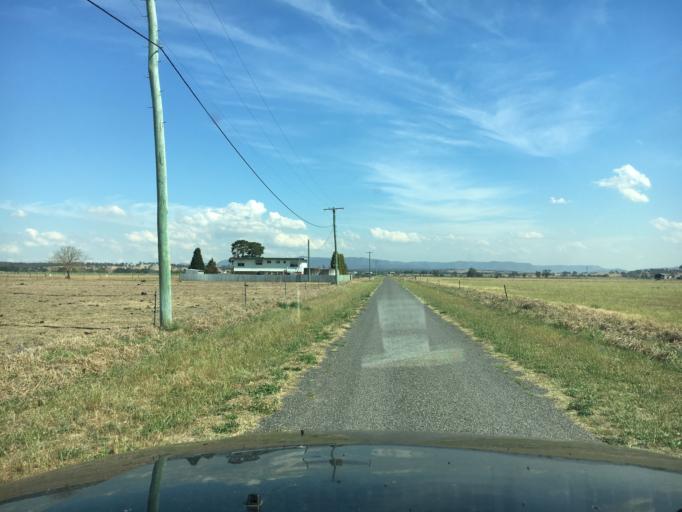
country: AU
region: New South Wales
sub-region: Singleton
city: Singleton
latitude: -32.5990
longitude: 151.2274
